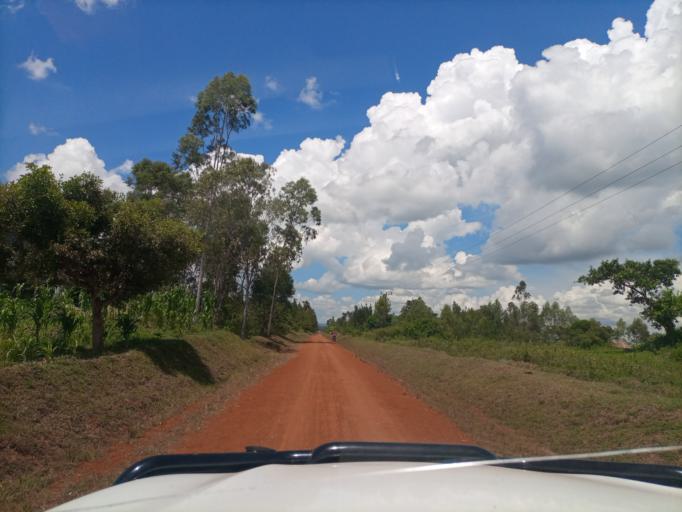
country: UG
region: Eastern Region
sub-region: Tororo District
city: Tororo
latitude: 0.6619
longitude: 34.0010
